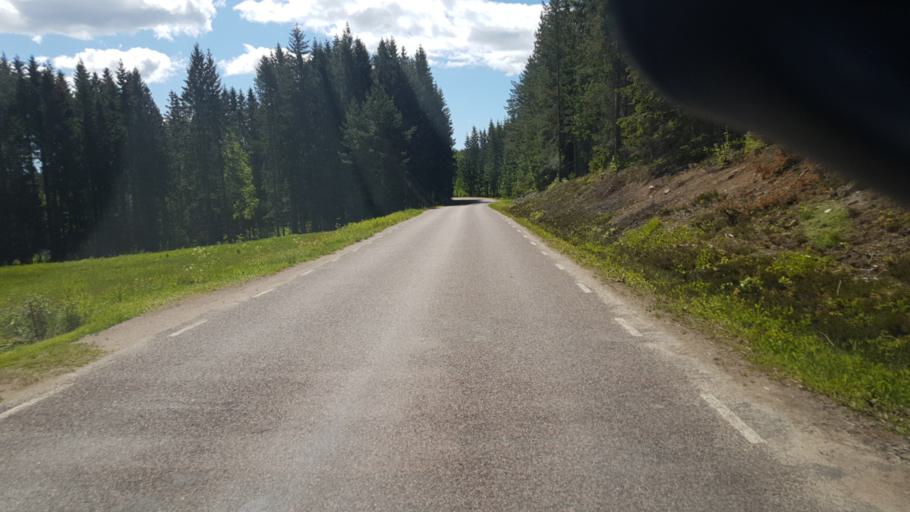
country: SE
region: Vaermland
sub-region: Grums Kommun
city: Grums
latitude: 59.5048
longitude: 12.8711
